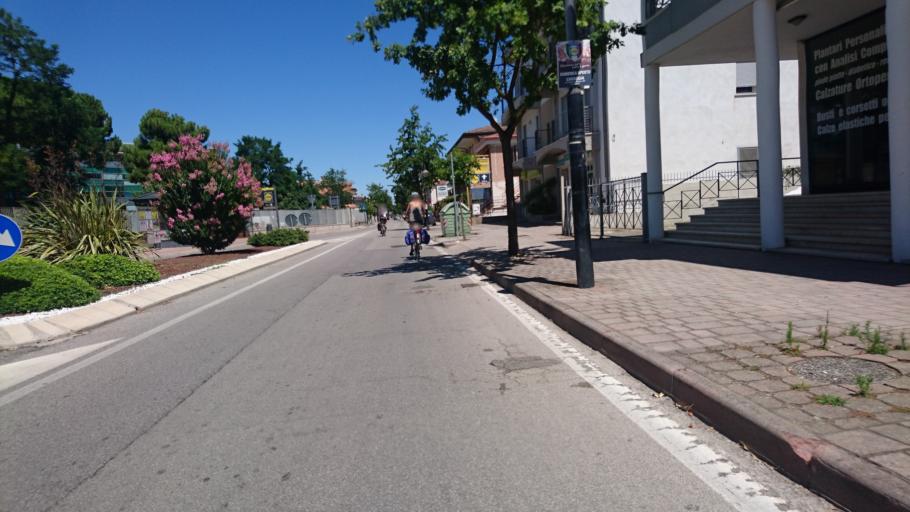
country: IT
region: Veneto
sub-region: Provincia di Venezia
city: Chioggia
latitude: 45.1984
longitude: 12.2850
